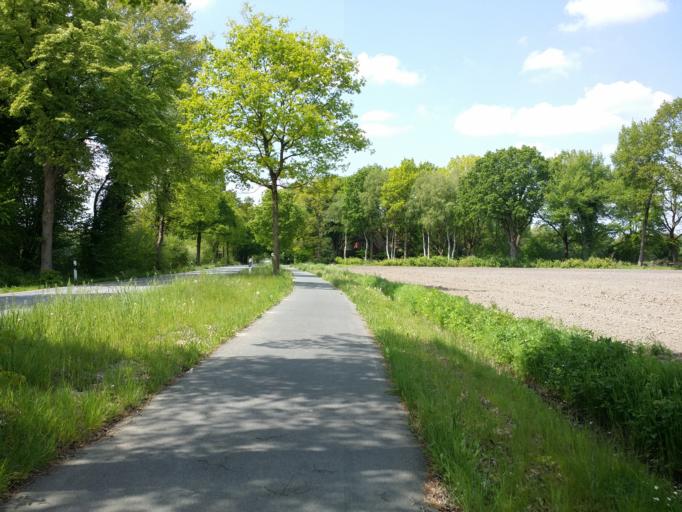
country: DE
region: Lower Saxony
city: Lubberstedt
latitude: 53.2965
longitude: 8.7846
